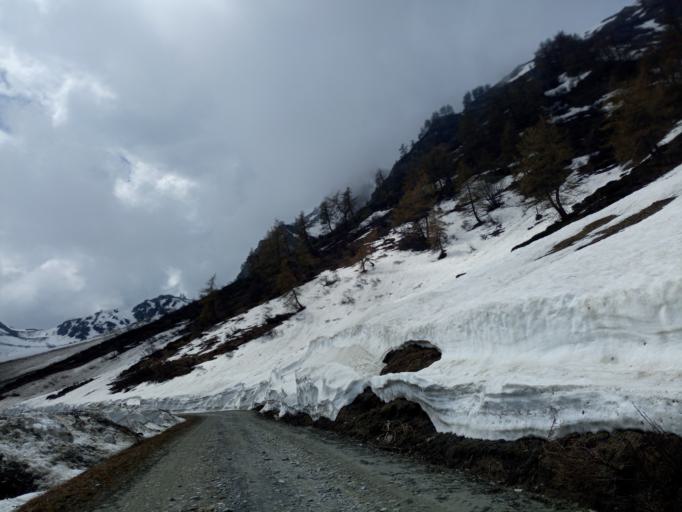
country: IT
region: Piedmont
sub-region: Provincia di Torino
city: Usseaux
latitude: 45.0806
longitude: 7.0538
